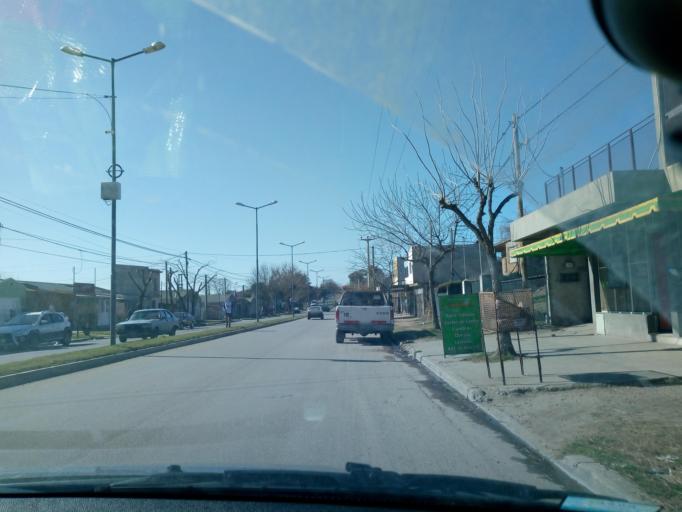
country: AR
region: Buenos Aires
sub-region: Partido de Tandil
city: Tandil
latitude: -37.3396
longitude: -59.1478
